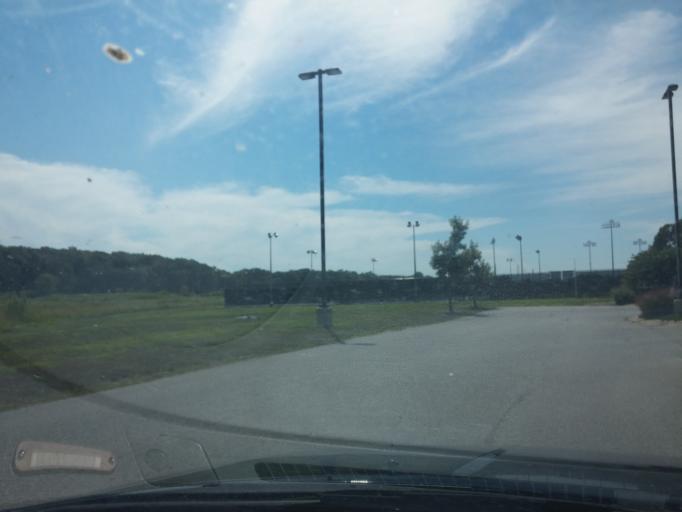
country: US
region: Indiana
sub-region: Tippecanoe County
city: West Lafayette
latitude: 40.4361
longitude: -86.9367
